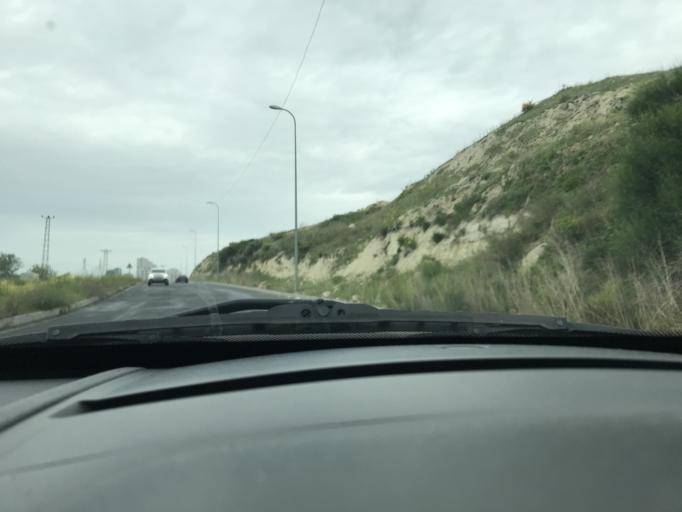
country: TR
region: Istanbul
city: Esenyurt
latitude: 41.0936
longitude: 28.6802
